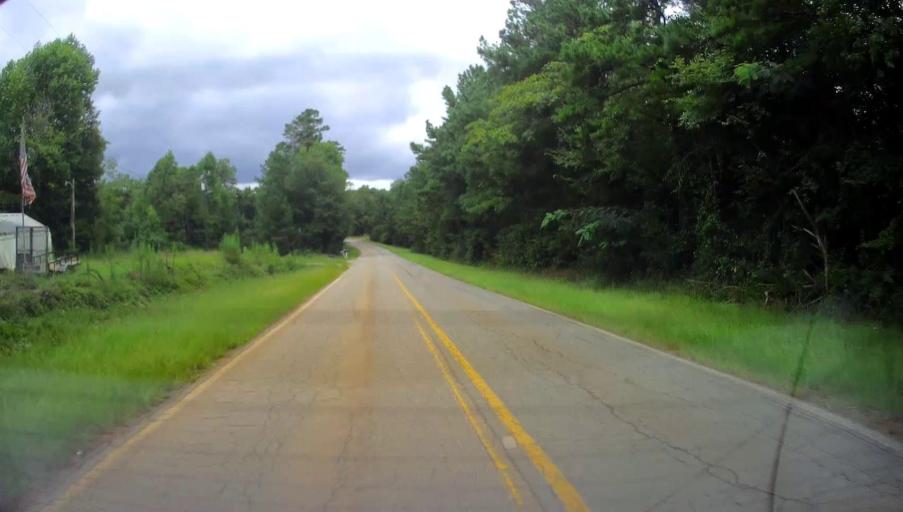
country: US
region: Georgia
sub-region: Bibb County
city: Macon
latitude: 32.7726
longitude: -83.5062
